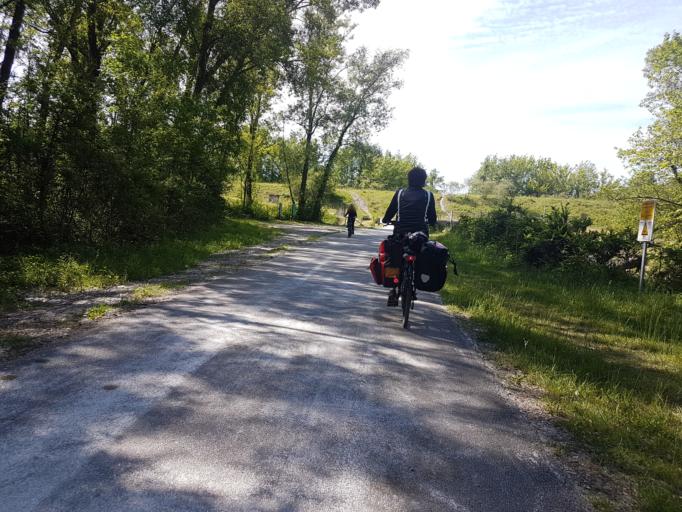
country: FR
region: Rhone-Alpes
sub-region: Departement de l'Ardeche
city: La Voulte-sur-Rhone
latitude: 44.7735
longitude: 4.7674
